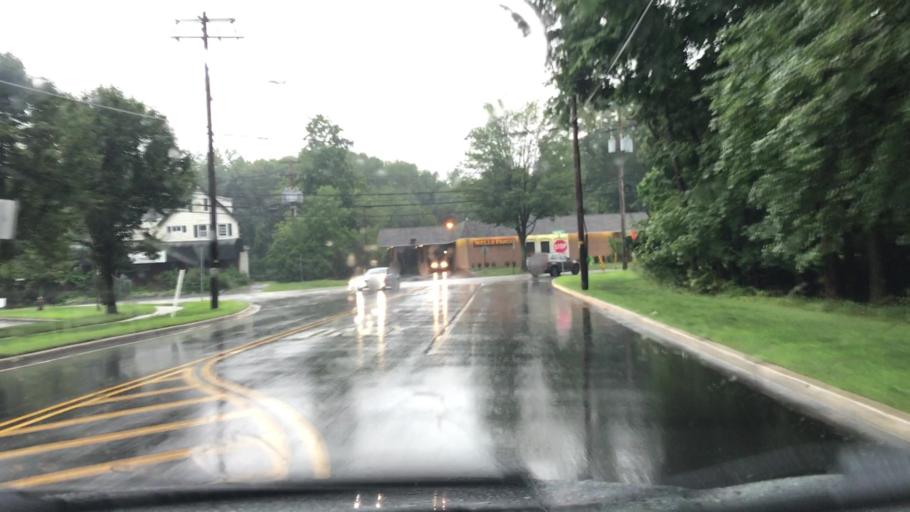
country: US
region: New Jersey
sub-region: Bergen County
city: Closter
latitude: 40.9678
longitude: -73.9542
